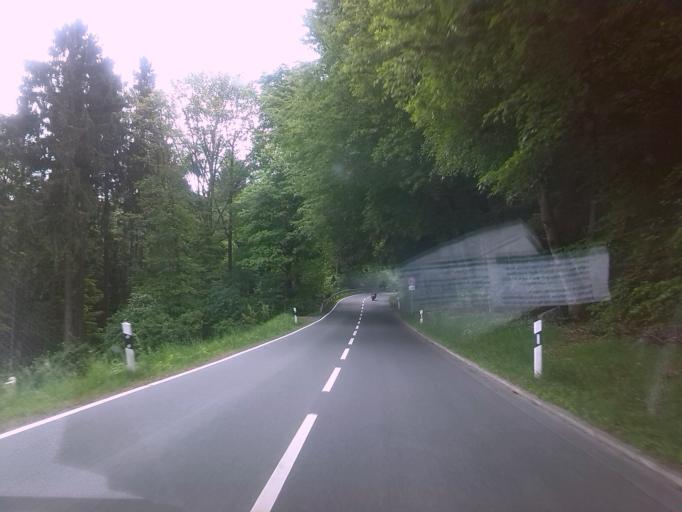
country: DE
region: Hesse
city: Lutzelbach
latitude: 49.7299
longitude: 8.7798
